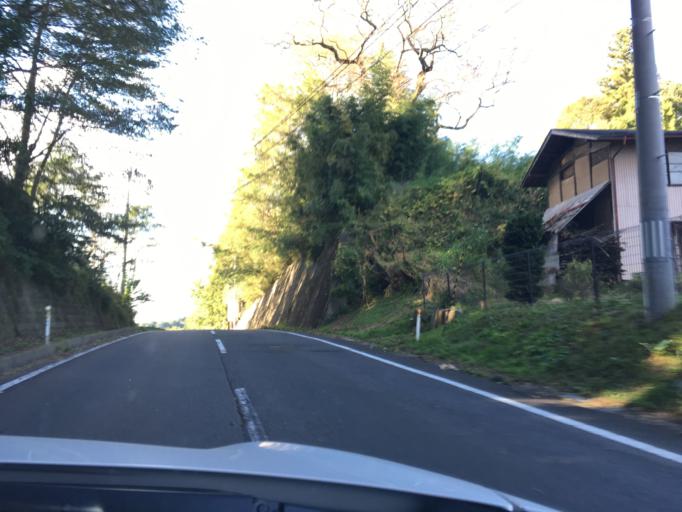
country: JP
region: Fukushima
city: Ishikawa
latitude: 37.2102
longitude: 140.4539
